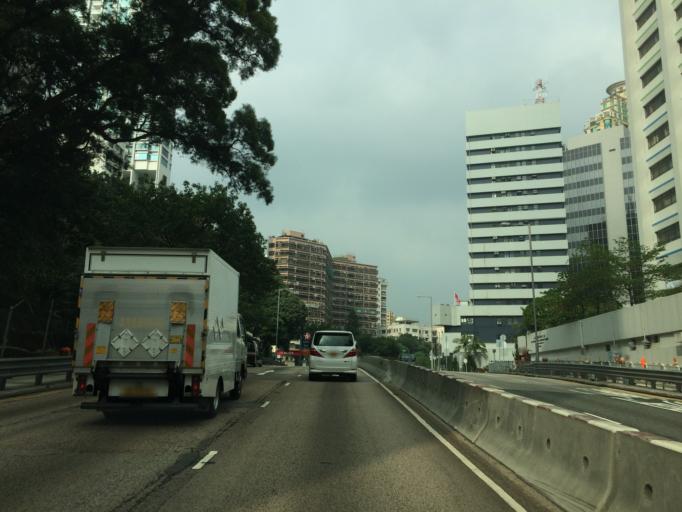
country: HK
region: Kowloon City
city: Kowloon
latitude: 22.3144
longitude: 114.1769
